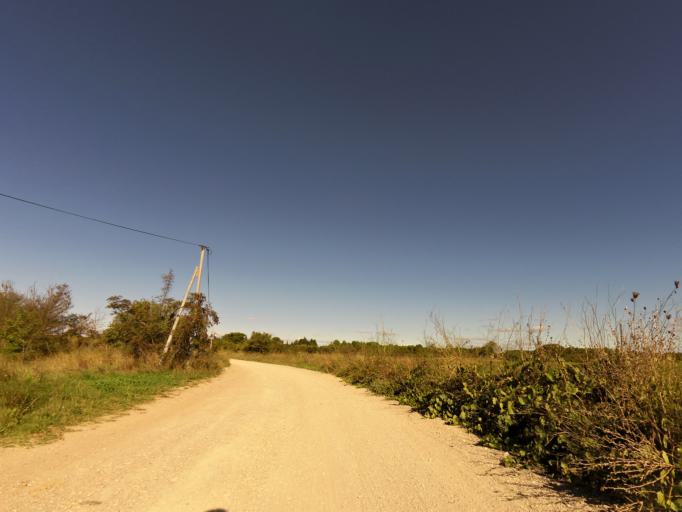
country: FR
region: Languedoc-Roussillon
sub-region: Departement du Gard
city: Gallargues-le-Montueux
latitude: 43.7250
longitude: 4.1573
